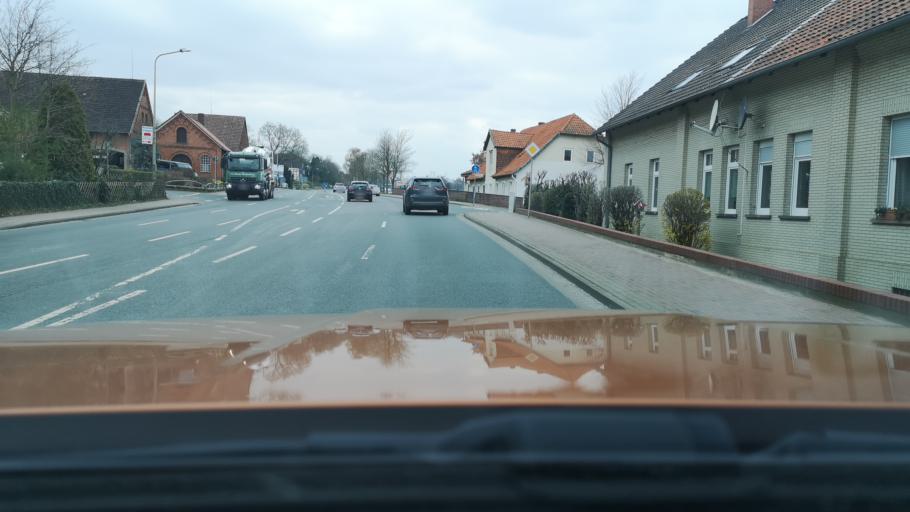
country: DE
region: Lower Saxony
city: Nienstadt
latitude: 52.2927
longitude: 9.1648
